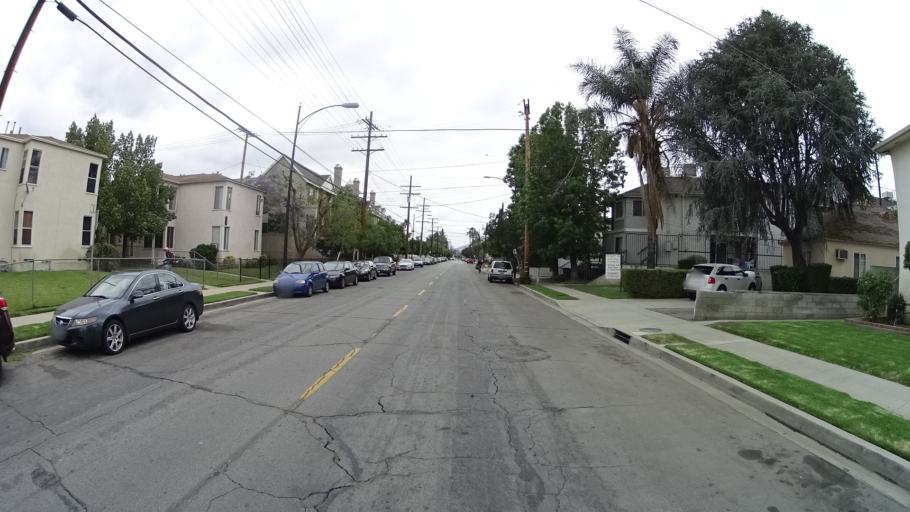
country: US
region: California
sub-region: Los Angeles County
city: Burbank
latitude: 34.1946
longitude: -118.3237
